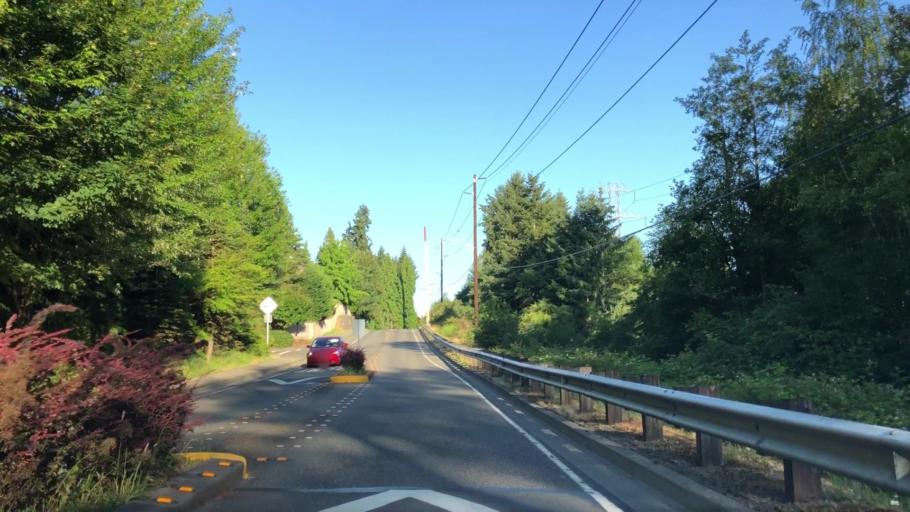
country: US
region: Washington
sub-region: King County
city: Redmond
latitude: 47.6995
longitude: -122.1157
